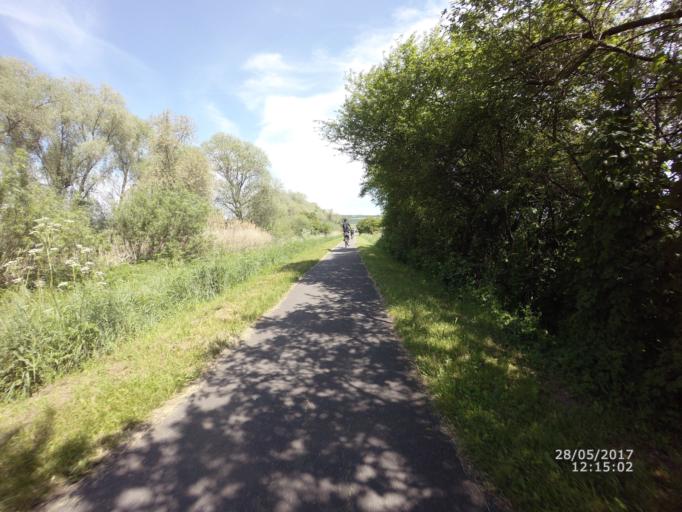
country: DE
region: Thuringia
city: Gorsleben
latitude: 51.2705
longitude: 11.1762
